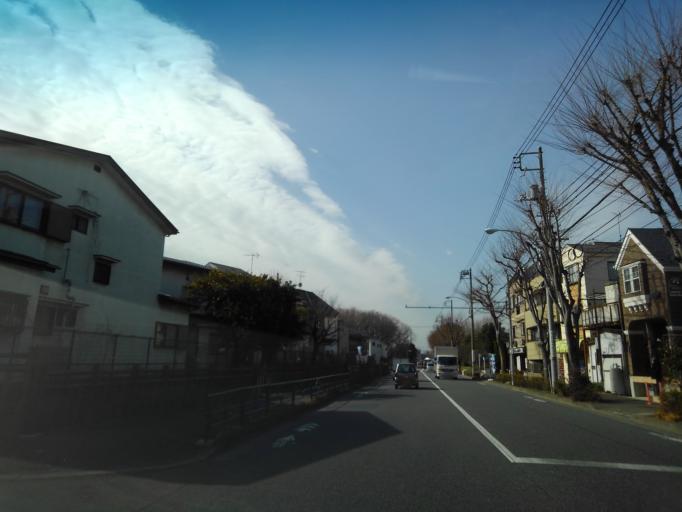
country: JP
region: Tokyo
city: Tanashicho
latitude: 35.7647
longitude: 139.5140
